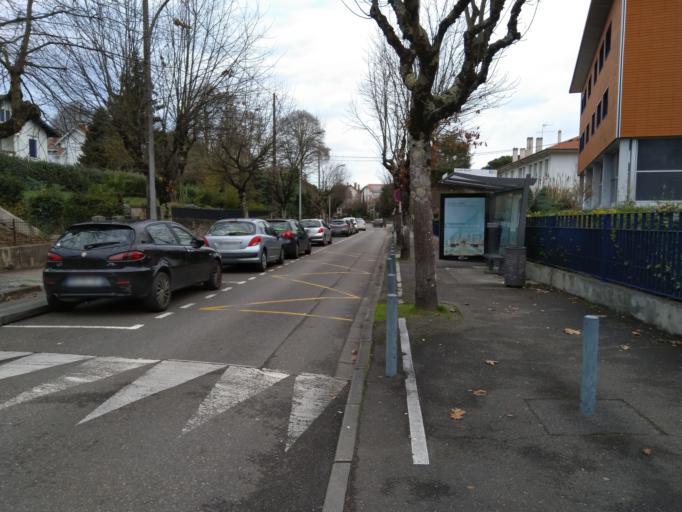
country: FR
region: Aquitaine
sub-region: Departement des Landes
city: Dax
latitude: 43.7026
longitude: -1.0565
